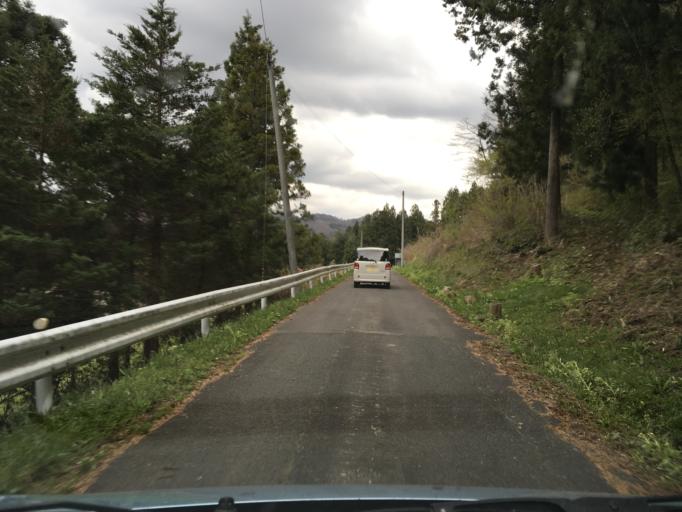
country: JP
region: Iwate
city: Ichinoseki
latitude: 38.9641
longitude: 141.2097
